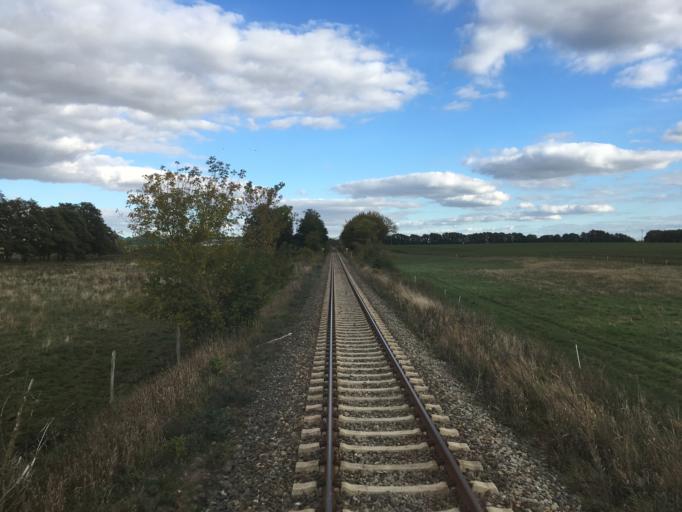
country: DE
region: Mecklenburg-Vorpommern
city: Grabowhofe
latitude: 53.5407
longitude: 12.5949
